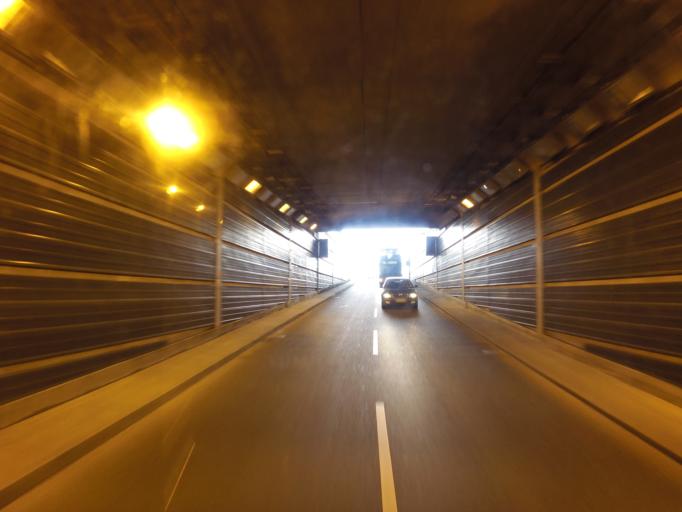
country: DE
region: Berlin
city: Tiergarten Bezirk
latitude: 52.5248
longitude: 13.3679
